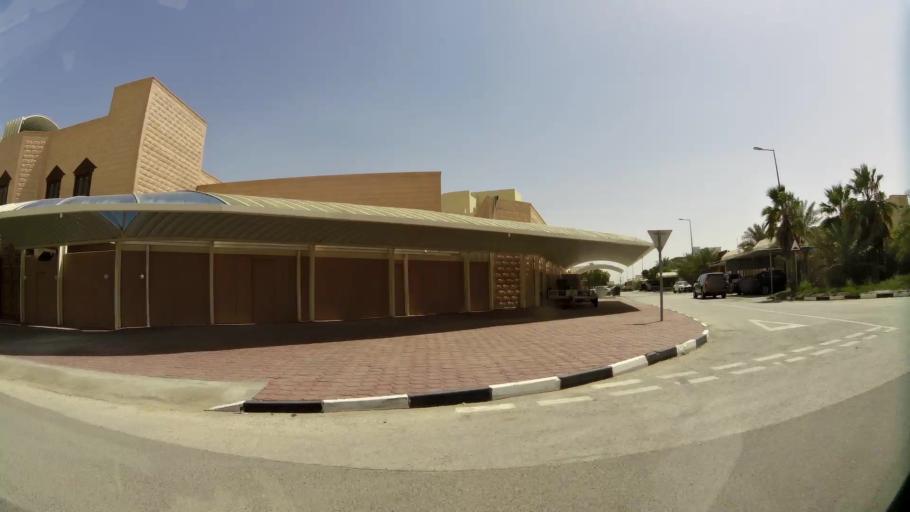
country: QA
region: Baladiyat Umm Salal
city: Umm Salal Muhammad
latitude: 25.3703
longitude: 51.4271
